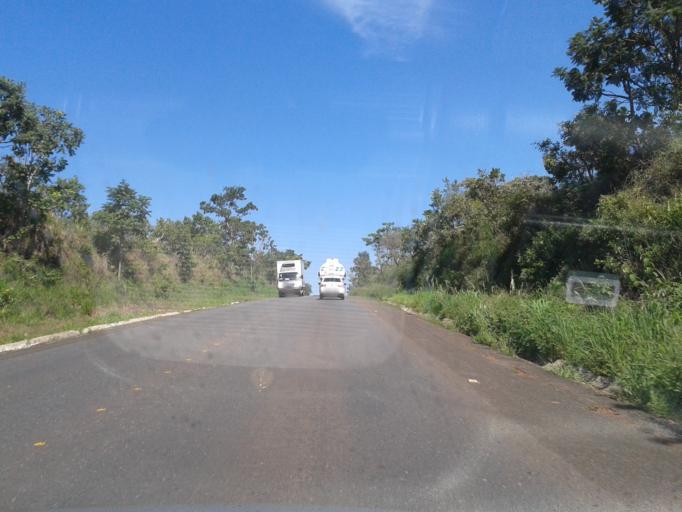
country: BR
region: Goias
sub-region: Bela Vista De Goias
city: Bela Vista de Goias
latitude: -17.0824
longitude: -48.8958
